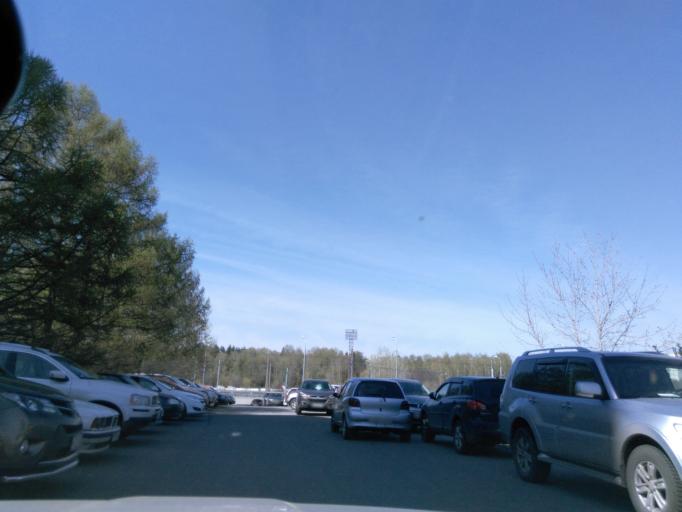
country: RU
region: Moscow
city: Zelenograd
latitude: 55.9854
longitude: 37.2136
